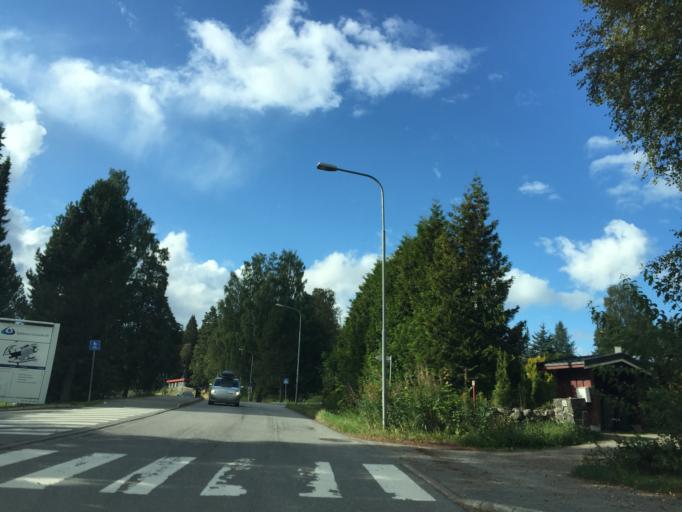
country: NO
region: Hedmark
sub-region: Kongsvinger
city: Kongsvinger
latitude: 60.1949
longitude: 11.9955
